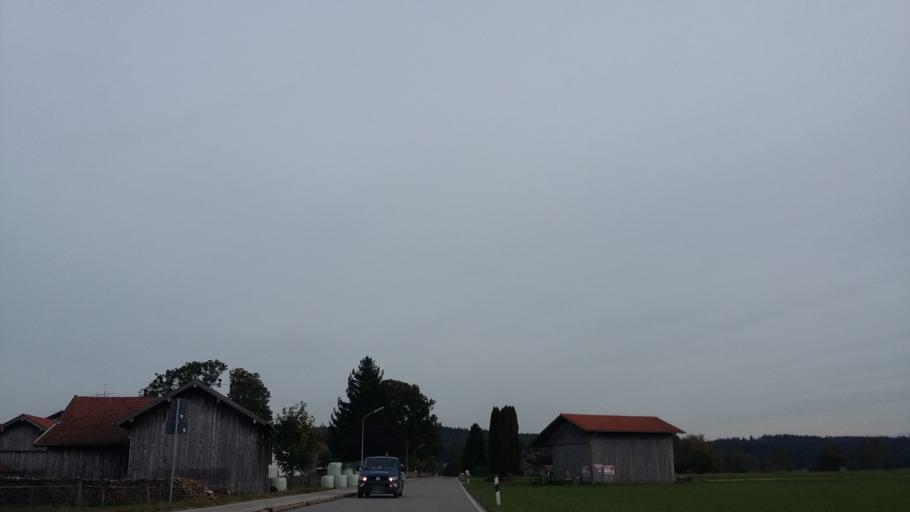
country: DE
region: Bavaria
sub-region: Upper Bavaria
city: Munsing
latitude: 47.9324
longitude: 11.3842
